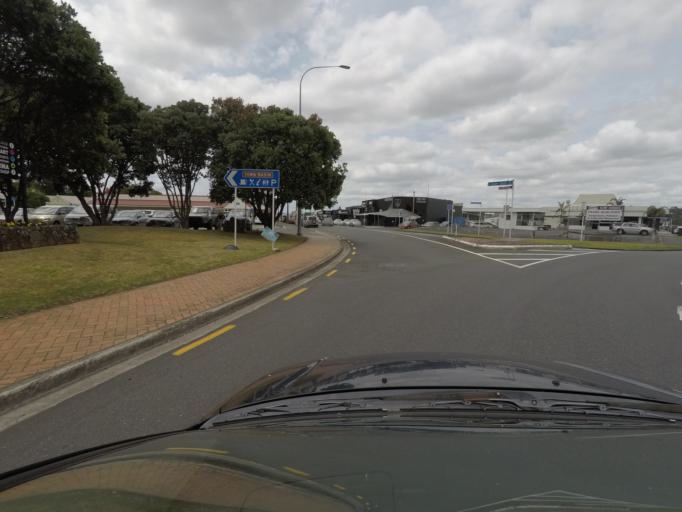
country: NZ
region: Northland
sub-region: Whangarei
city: Whangarei
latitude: -35.7256
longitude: 174.3263
